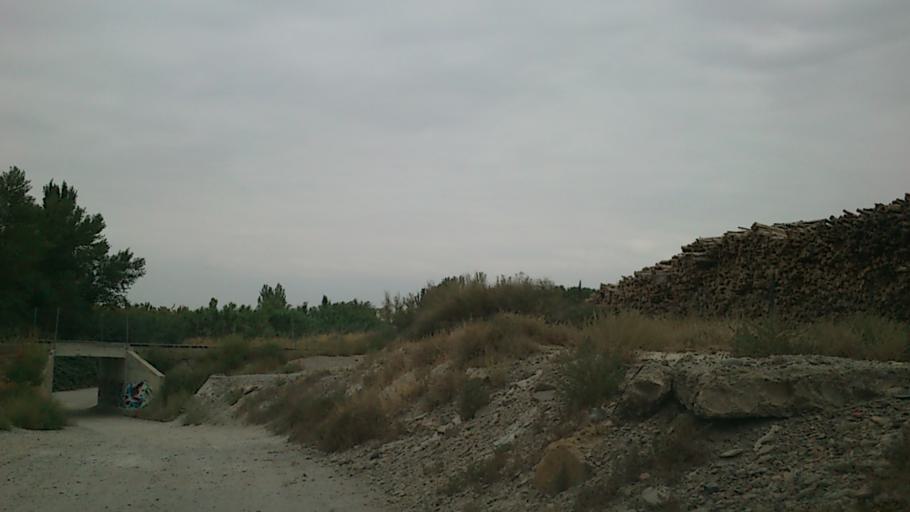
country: ES
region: Aragon
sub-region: Provincia de Zaragoza
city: Zaragoza
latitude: 41.6974
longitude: -0.8304
